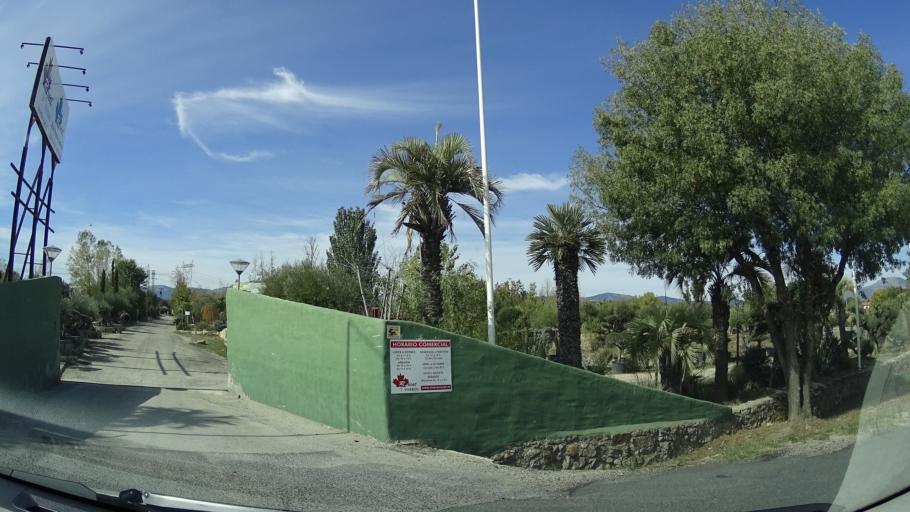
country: ES
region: Madrid
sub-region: Provincia de Madrid
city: Navalquejigo
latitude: 40.6151
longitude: -4.0243
